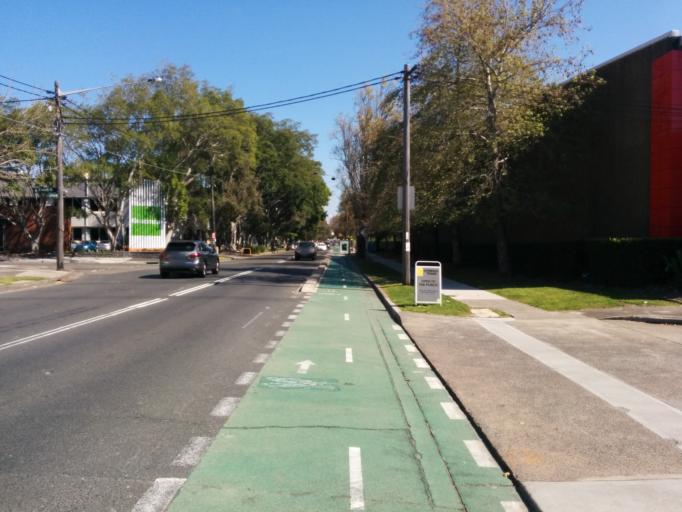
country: AU
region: New South Wales
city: Alexandria
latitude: -33.9138
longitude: 151.1922
